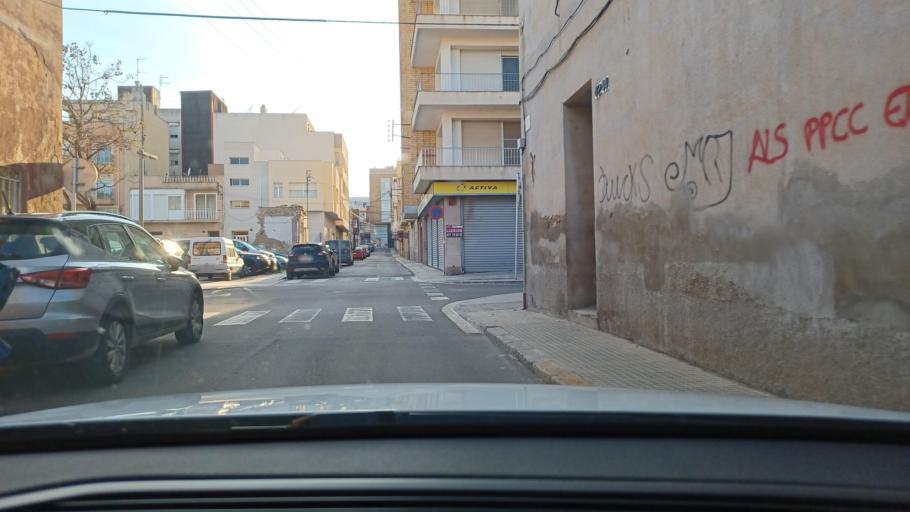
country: ES
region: Catalonia
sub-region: Provincia de Tarragona
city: Amposta
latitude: 40.7097
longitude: 0.5776
